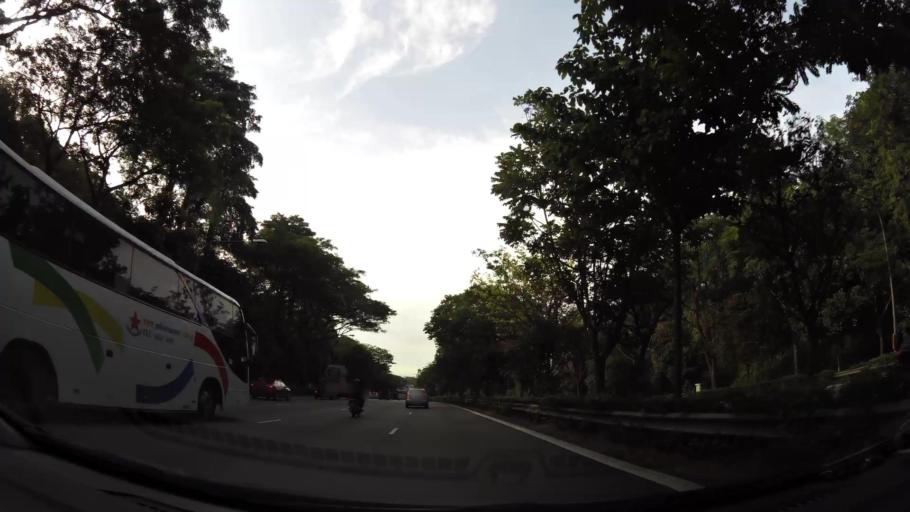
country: MY
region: Johor
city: Johor Bahru
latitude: 1.3374
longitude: 103.6771
